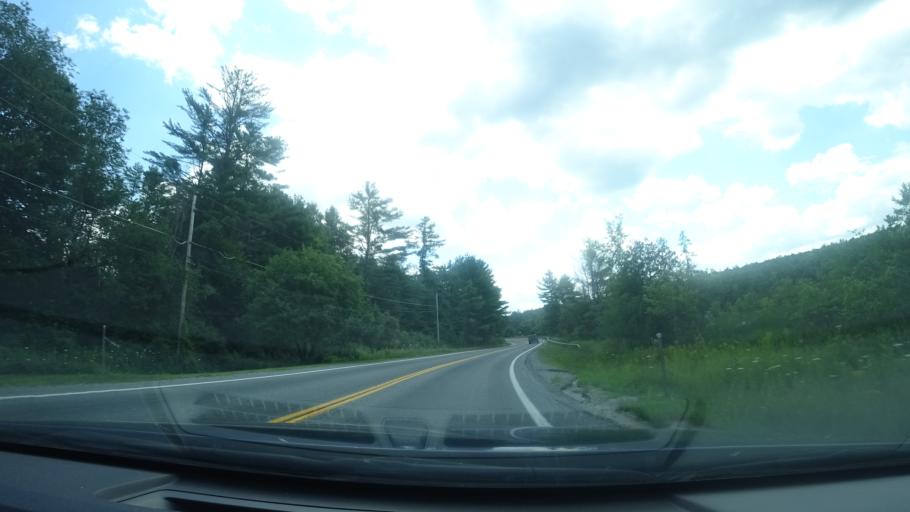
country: US
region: New York
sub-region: Warren County
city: Warrensburg
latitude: 43.6628
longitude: -73.8216
